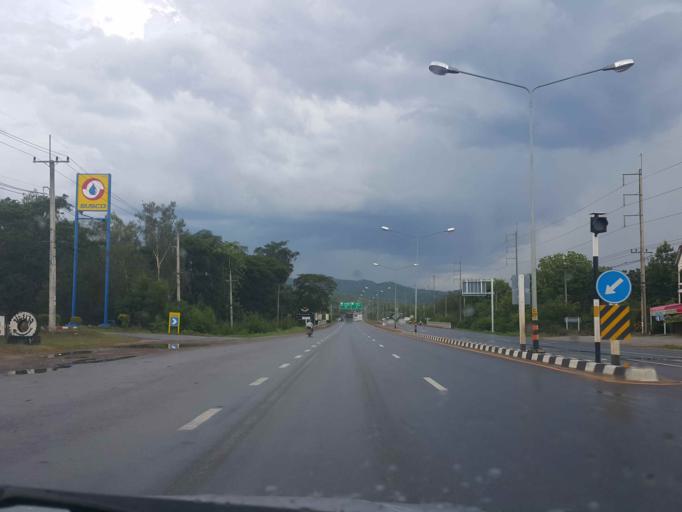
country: TH
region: Phrae
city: Den Chai
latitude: 17.9724
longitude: 100.0750
